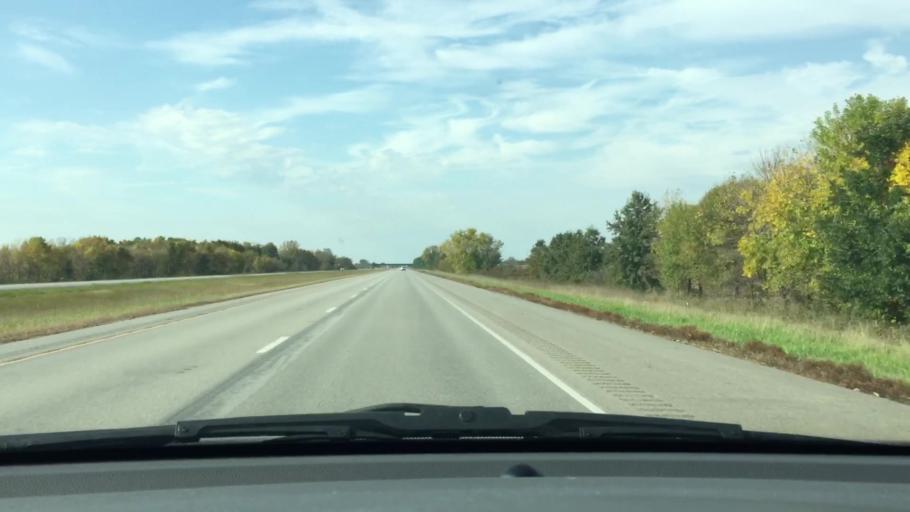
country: US
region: Illinois
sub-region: Rock Island County
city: Port Byron
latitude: 41.5685
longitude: -90.2267
